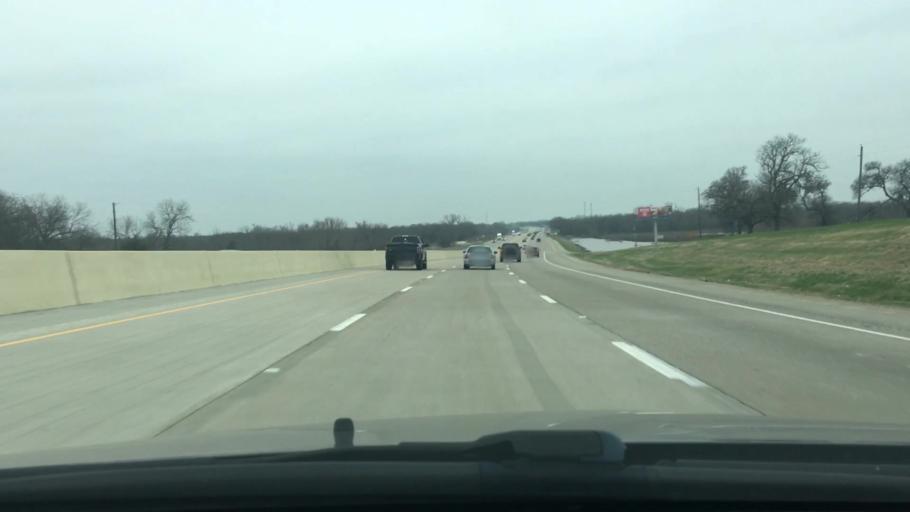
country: US
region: Texas
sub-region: Navarro County
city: Corsicana
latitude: 31.9566
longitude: -96.4205
